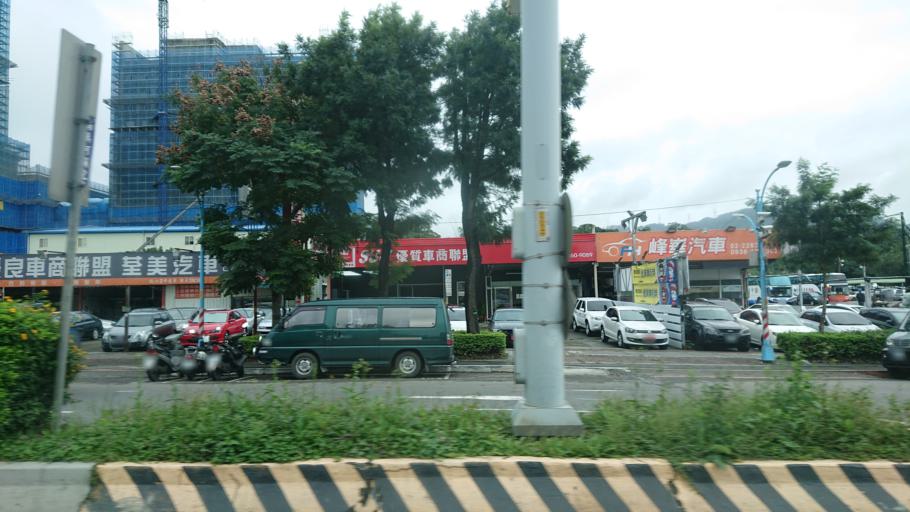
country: TW
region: Taipei
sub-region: Taipei
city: Banqiao
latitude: 24.9760
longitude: 121.4473
